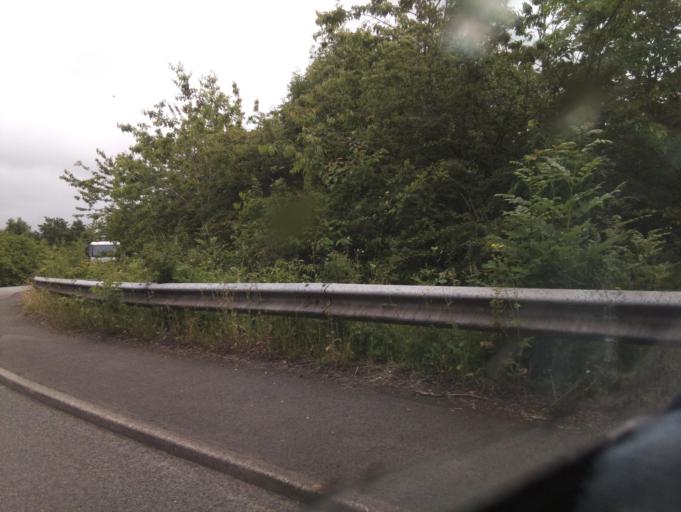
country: GB
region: England
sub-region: Derbyshire
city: Rodsley
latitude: 52.8798
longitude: -1.7005
